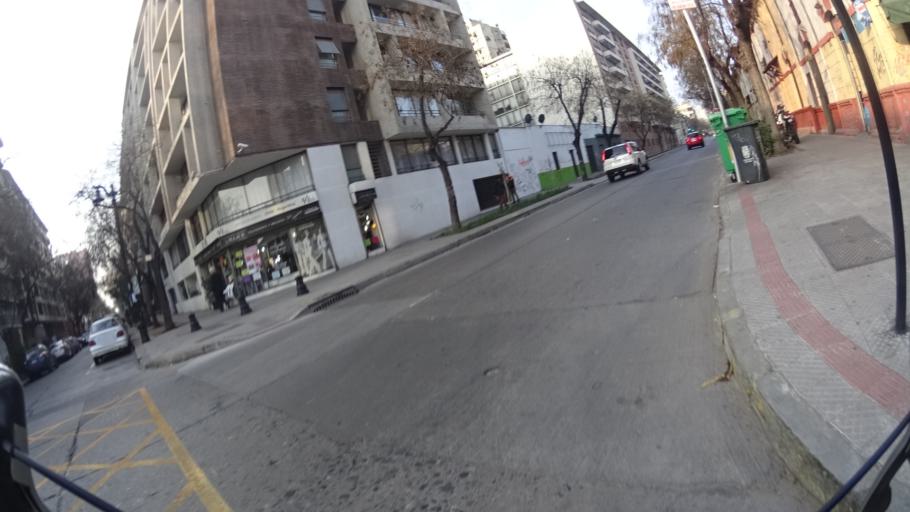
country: CL
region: Santiago Metropolitan
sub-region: Provincia de Santiago
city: Santiago
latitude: -33.4537
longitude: -70.6629
